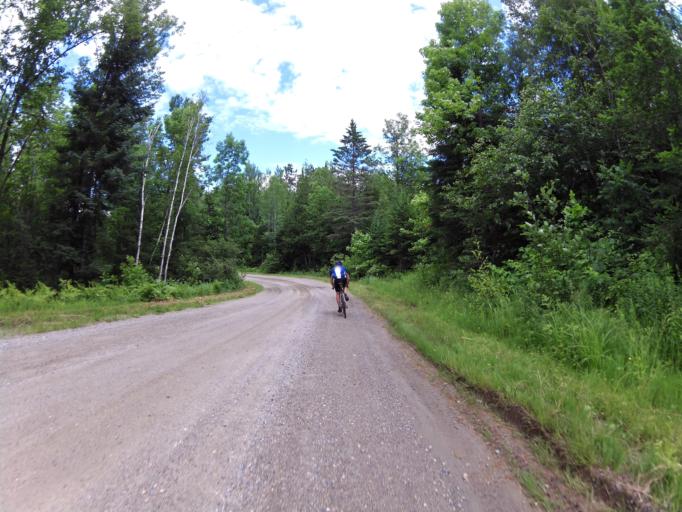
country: CA
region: Ontario
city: Renfrew
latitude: 45.1269
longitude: -76.6859
